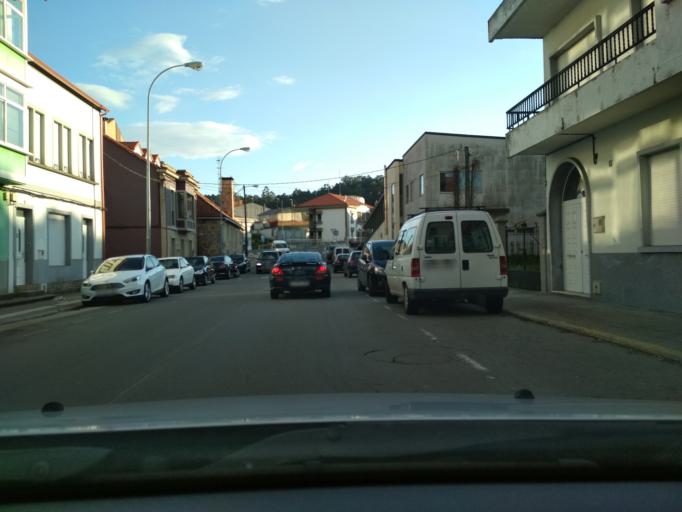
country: ES
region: Galicia
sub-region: Provincia da Coruna
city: Outes
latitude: 42.8437
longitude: -8.9072
